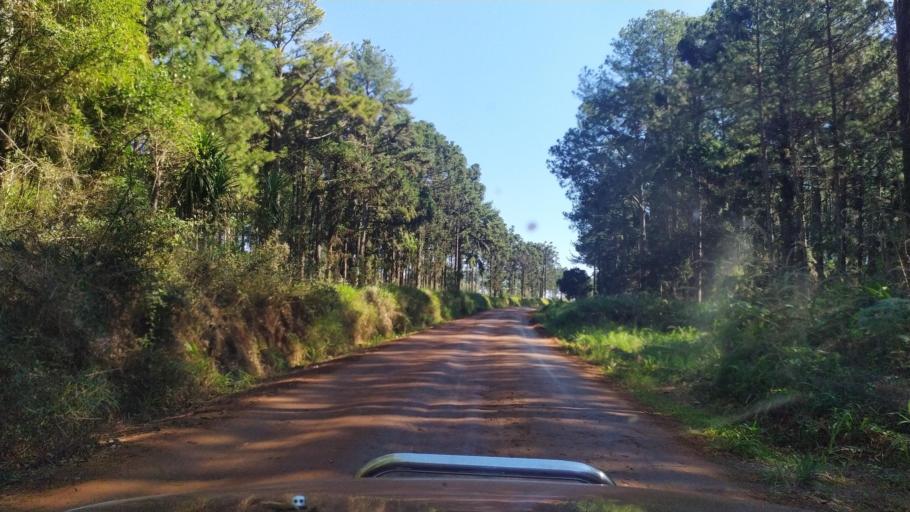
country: AR
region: Misiones
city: El Alcazar
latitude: -26.7157
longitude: -54.7093
